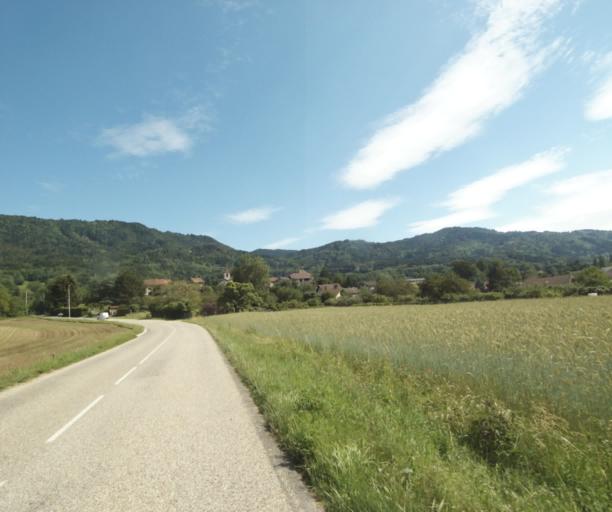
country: FR
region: Rhone-Alpes
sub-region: Departement de la Haute-Savoie
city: Perrignier
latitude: 46.2884
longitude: 6.4391
